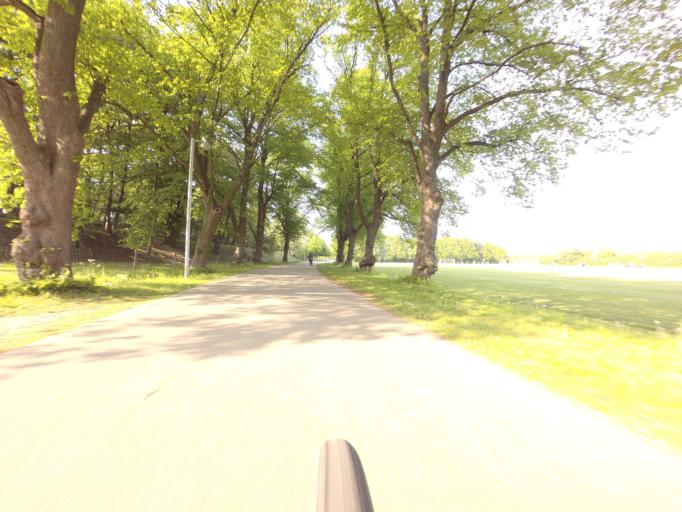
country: DK
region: Capital Region
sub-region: Glostrup Kommune
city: Glostrup
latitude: 55.6740
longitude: 12.4269
